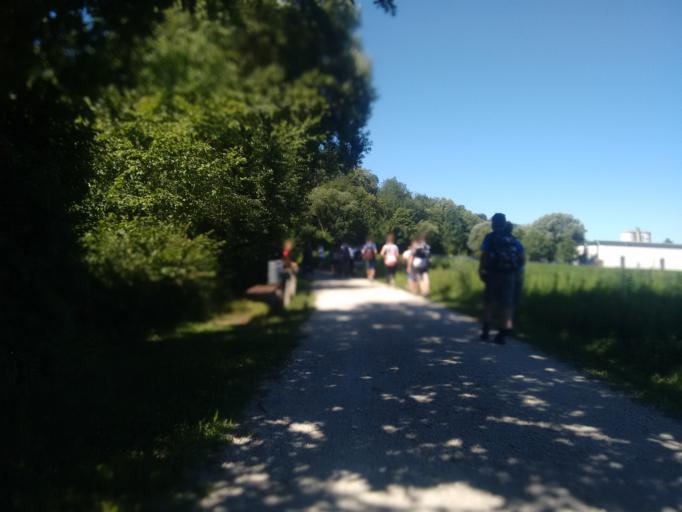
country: AT
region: Upper Austria
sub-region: Politischer Bezirk Grieskirchen
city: Bad Schallerbach
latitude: 48.2252
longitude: 13.9417
